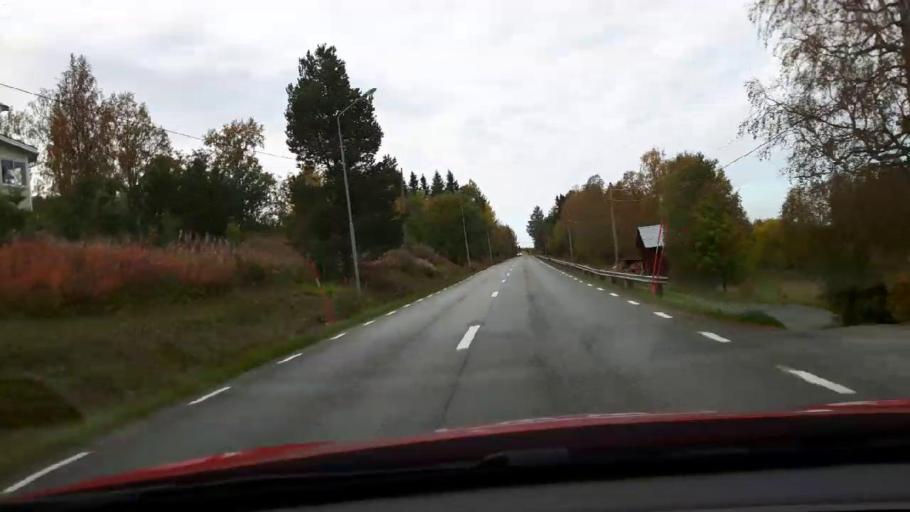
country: SE
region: Jaemtland
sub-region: Krokoms Kommun
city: Krokom
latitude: 63.1827
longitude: 14.0798
